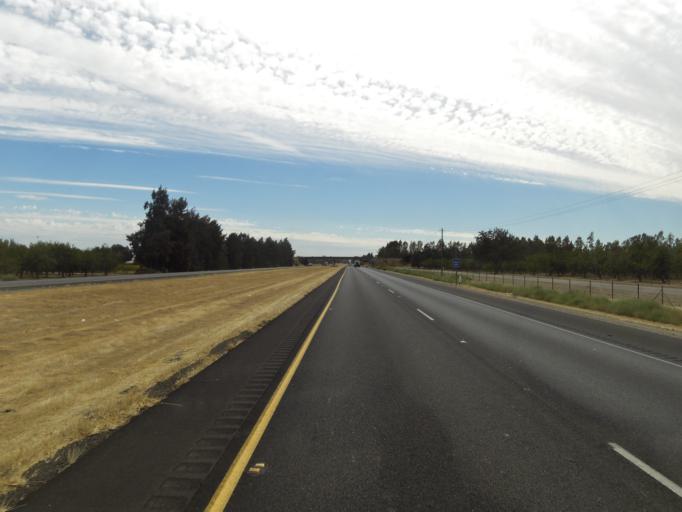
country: US
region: California
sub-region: Yolo County
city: Dunnigan
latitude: 38.9140
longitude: -121.9928
